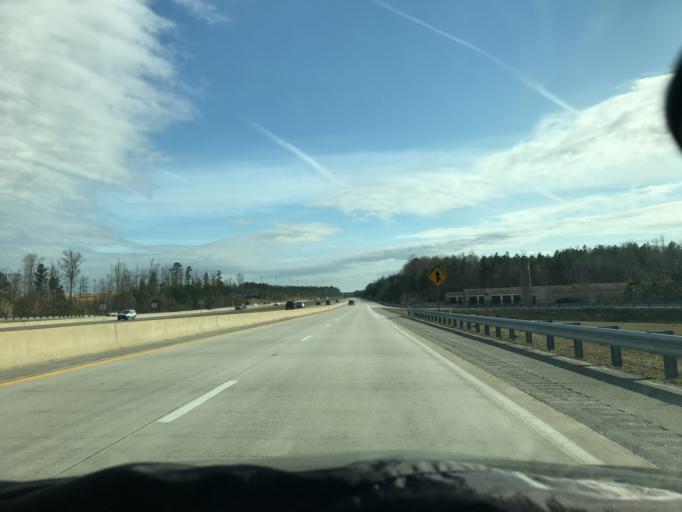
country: US
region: Virginia
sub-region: Chesterfield County
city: Brandermill
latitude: 37.4590
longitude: -77.6384
